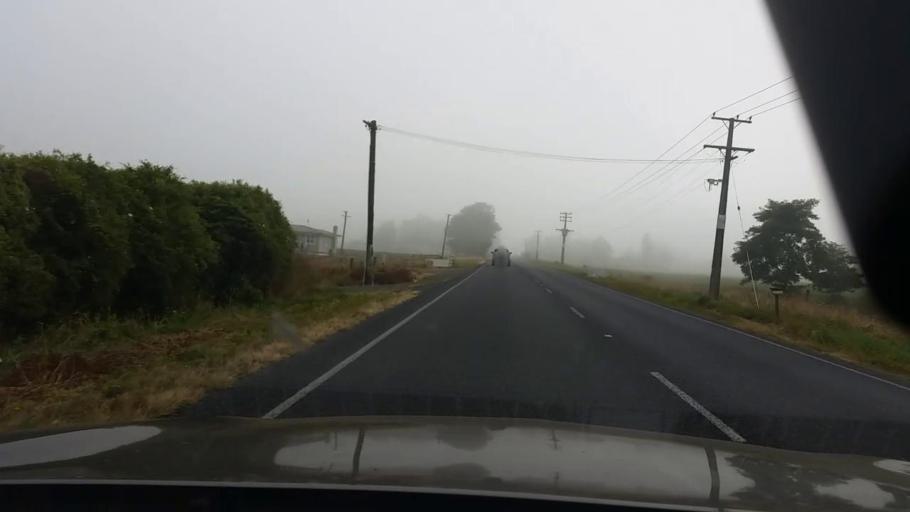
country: NZ
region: Waikato
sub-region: Hamilton City
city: Hamilton
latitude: -37.6337
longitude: 175.3058
